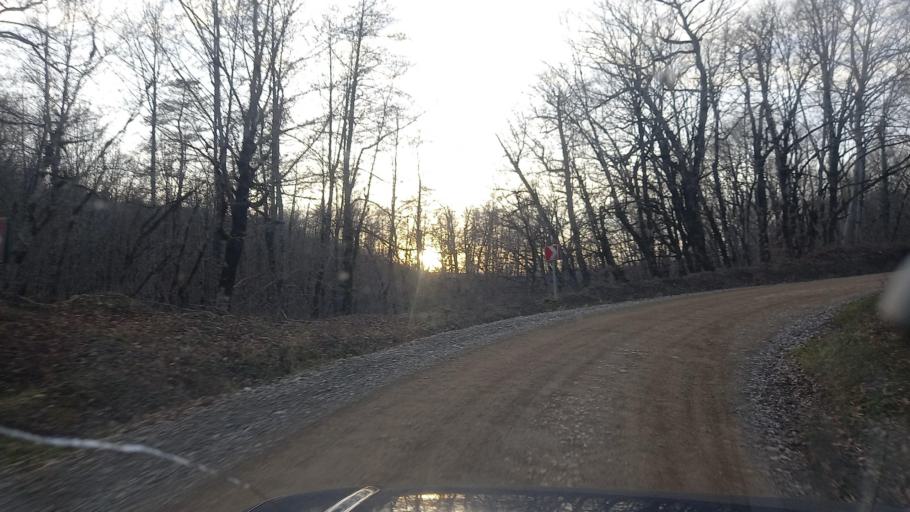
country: RU
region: Krasnodarskiy
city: Khadyzhensk
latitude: 44.3404
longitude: 39.2571
